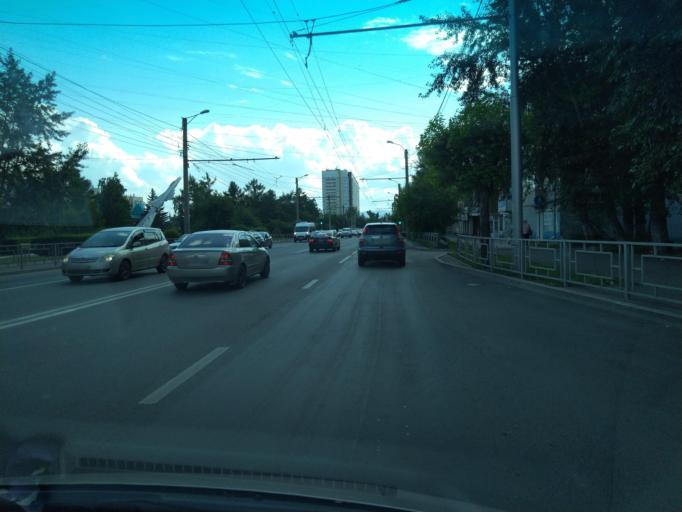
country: RU
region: Krasnoyarskiy
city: Solnechnyy
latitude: 56.0451
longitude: 92.9412
